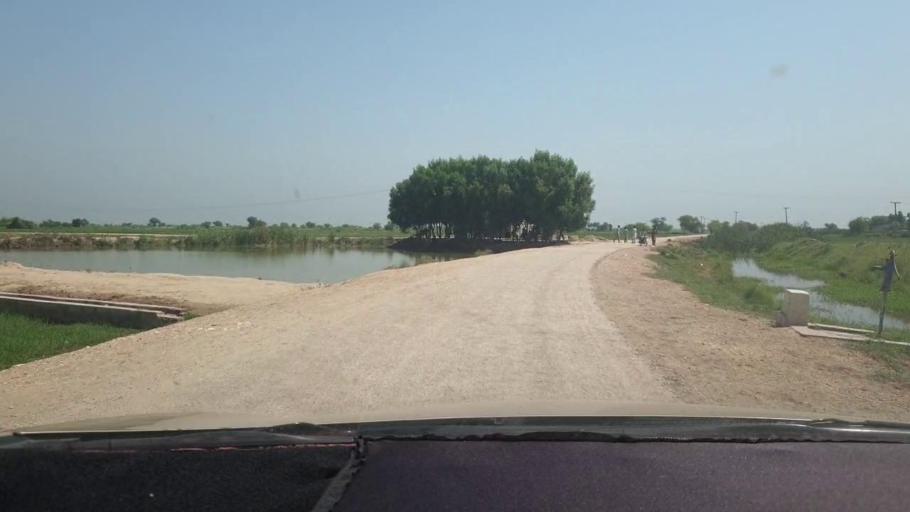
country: PK
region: Sindh
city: Miro Khan
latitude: 27.6845
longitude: 68.0942
